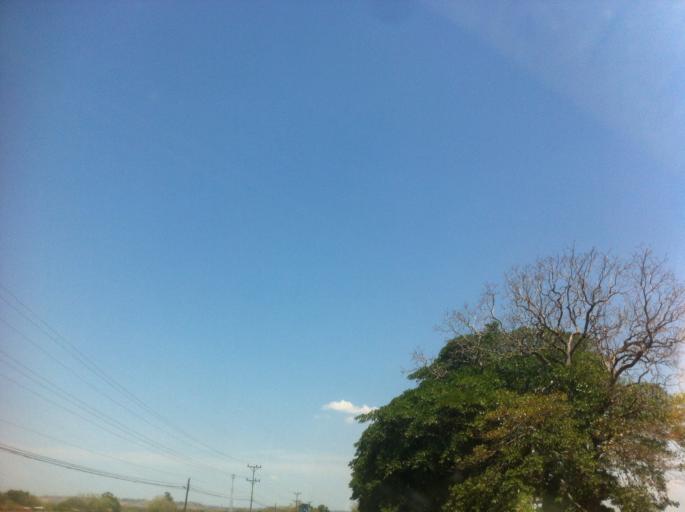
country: CR
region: Guanacaste
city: Sardinal
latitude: 10.5340
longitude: -85.5845
